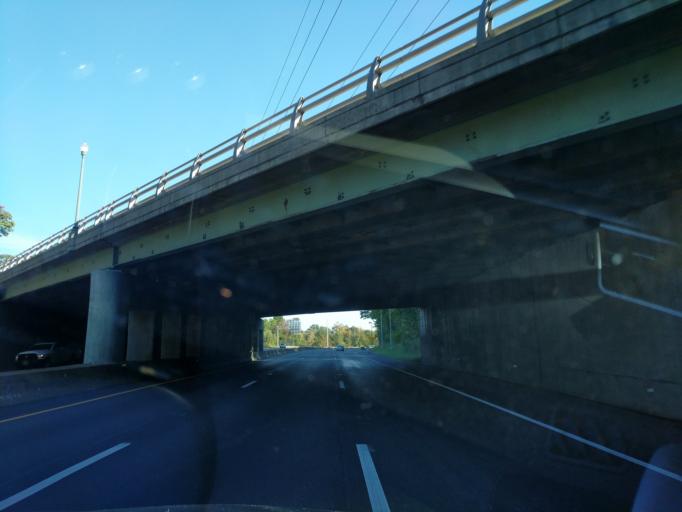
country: US
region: Virginia
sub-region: Henrico County
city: Lakeside
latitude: 37.5937
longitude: -77.4674
